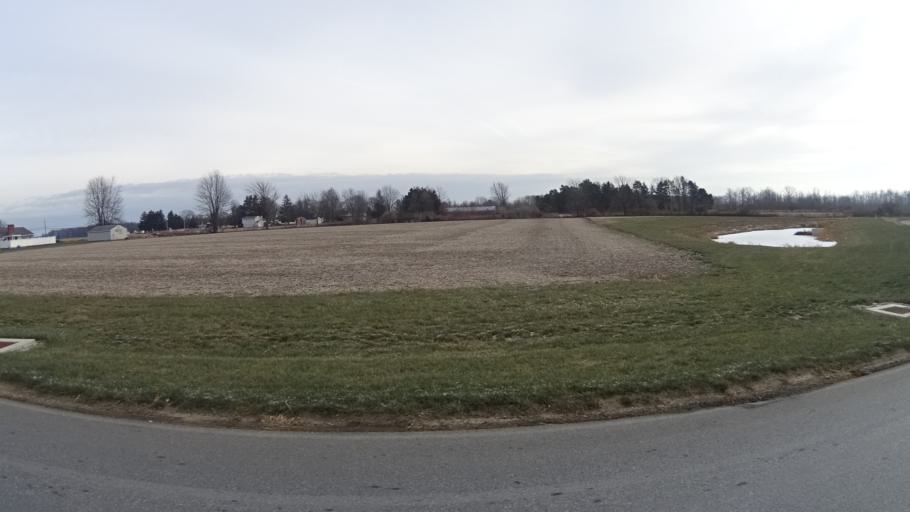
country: US
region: Ohio
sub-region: Lorain County
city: Lagrange
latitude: 41.2356
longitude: -82.1086
